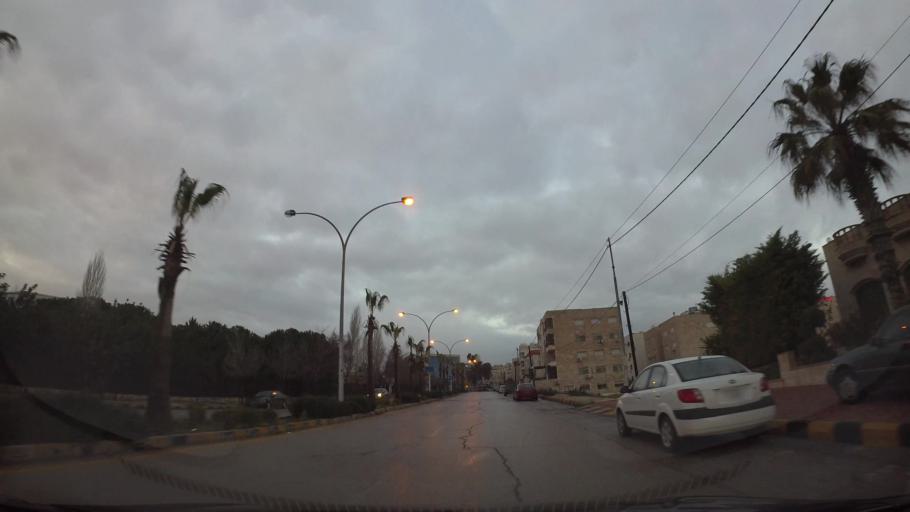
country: JO
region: Amman
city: Amman
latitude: 31.9876
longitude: 35.9102
